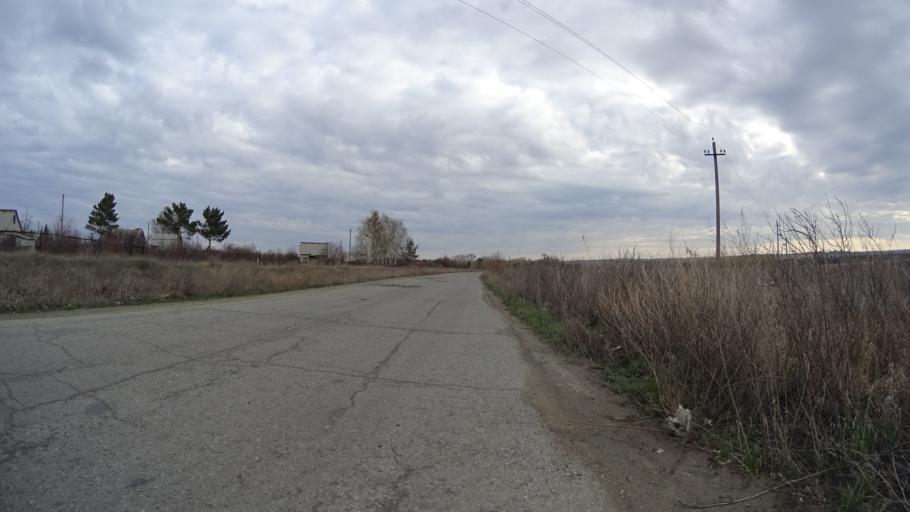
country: RU
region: Chelyabinsk
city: Troitsk
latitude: 54.0919
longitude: 61.4881
